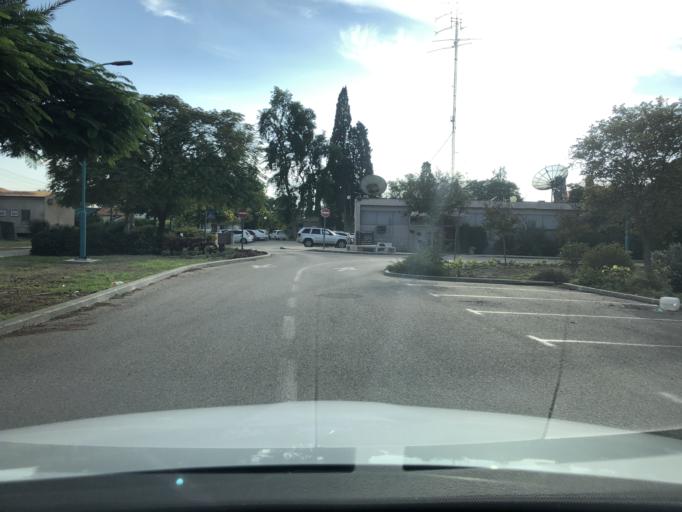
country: IL
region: Northern District
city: Yavne'el
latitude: 32.6613
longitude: 35.5833
